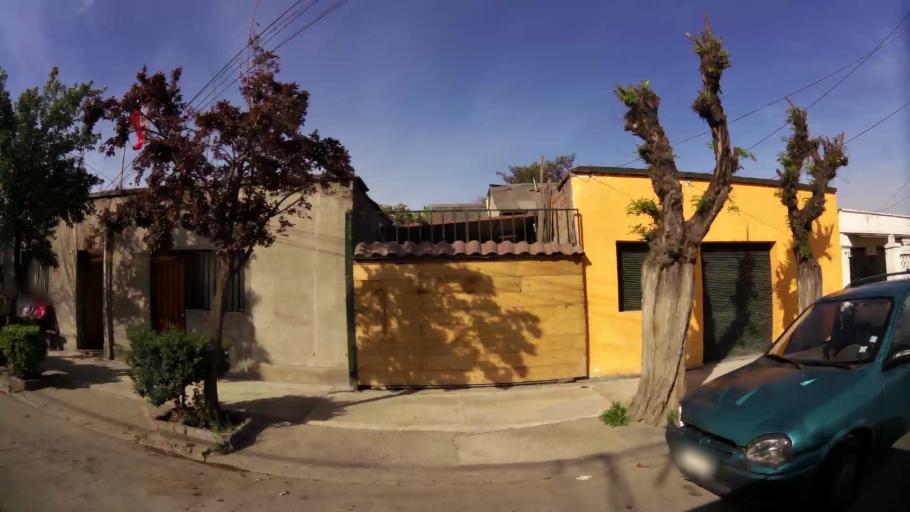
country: CL
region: Santiago Metropolitan
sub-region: Provincia de Santiago
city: Santiago
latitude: -33.5136
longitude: -70.6299
